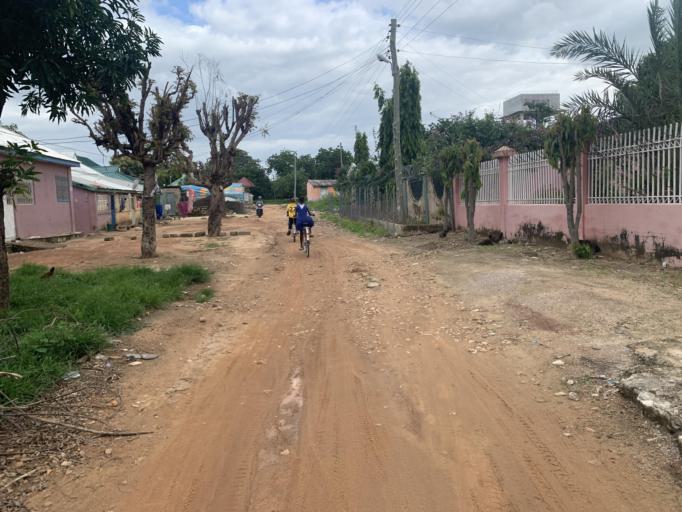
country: GH
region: Upper East
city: Navrongo
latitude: 10.9007
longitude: -1.0892
